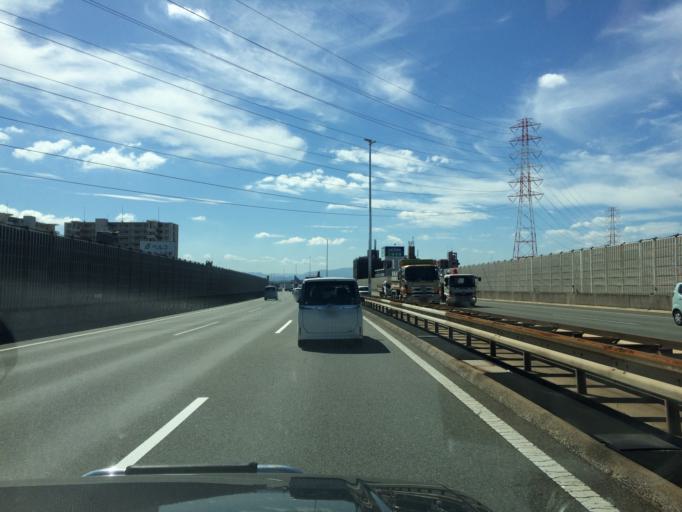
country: JP
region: Osaka
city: Yao
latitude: 34.6059
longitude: 135.5733
